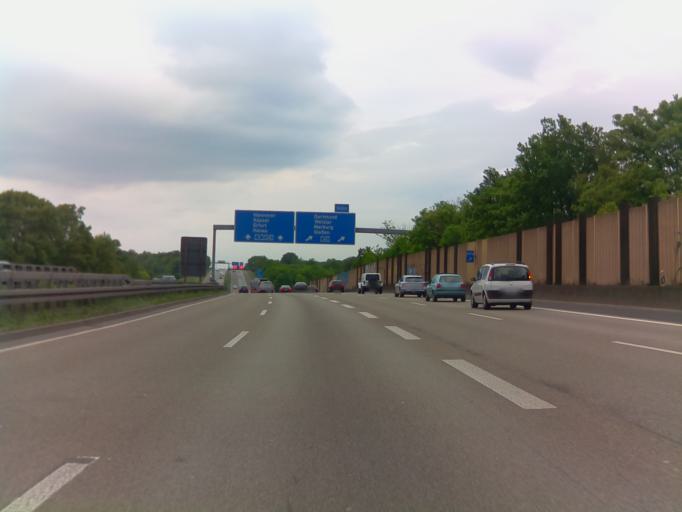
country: DE
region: Hesse
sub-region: Regierungsbezirk Darmstadt
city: Rockenberg
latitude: 50.4614
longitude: 8.7220
